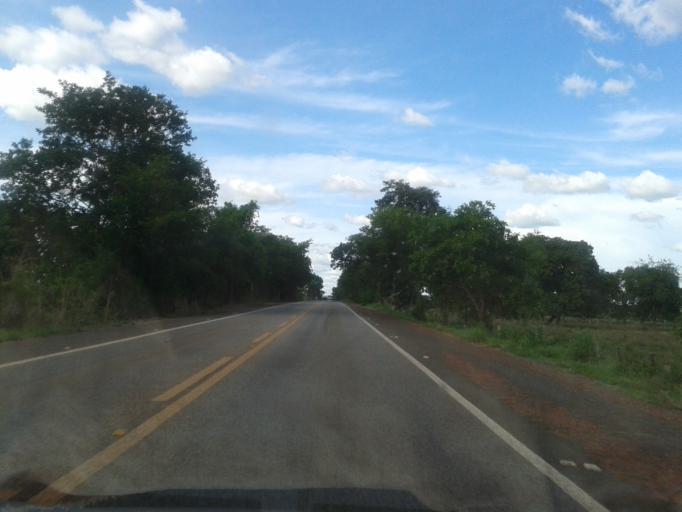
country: BR
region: Goias
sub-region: Mozarlandia
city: Mozarlandia
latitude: -15.0316
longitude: -50.6014
